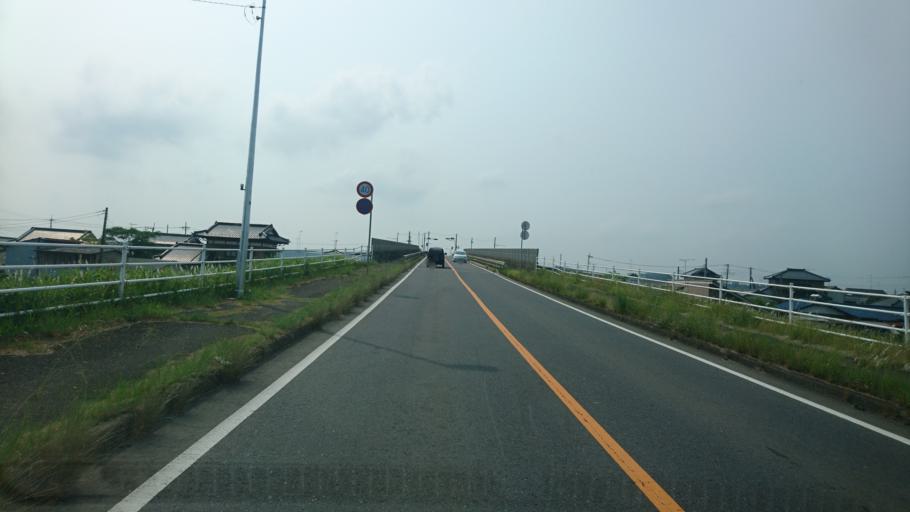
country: JP
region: Ibaraki
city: Edosaki
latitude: 35.8854
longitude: 140.3436
